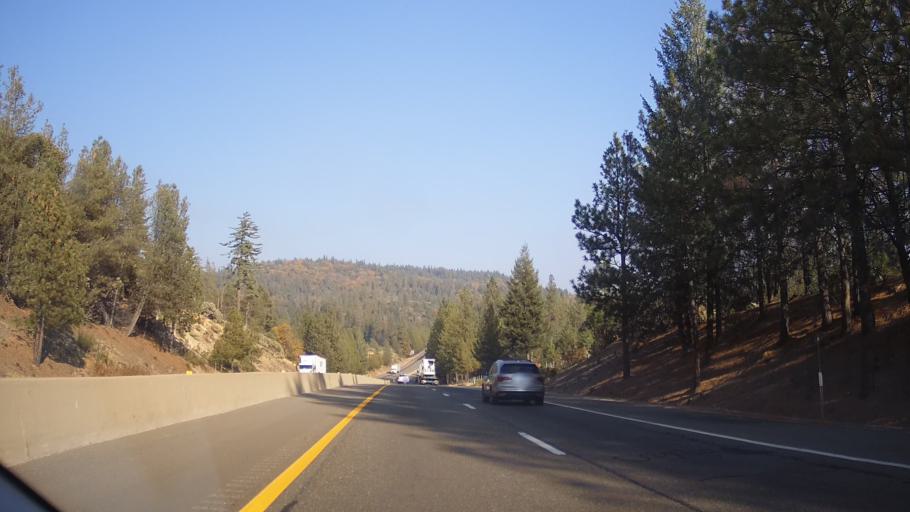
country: US
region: California
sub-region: Placer County
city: Colfax
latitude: 39.1553
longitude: -120.8864
